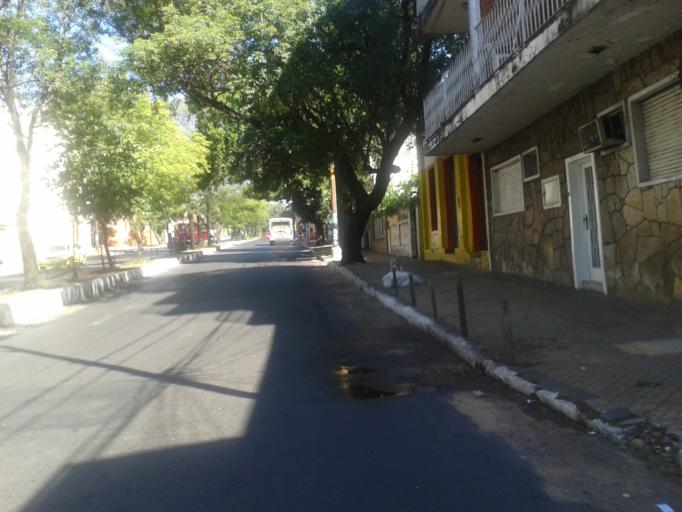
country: PY
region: Asuncion
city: Asuncion
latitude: -25.2919
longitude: -57.6376
